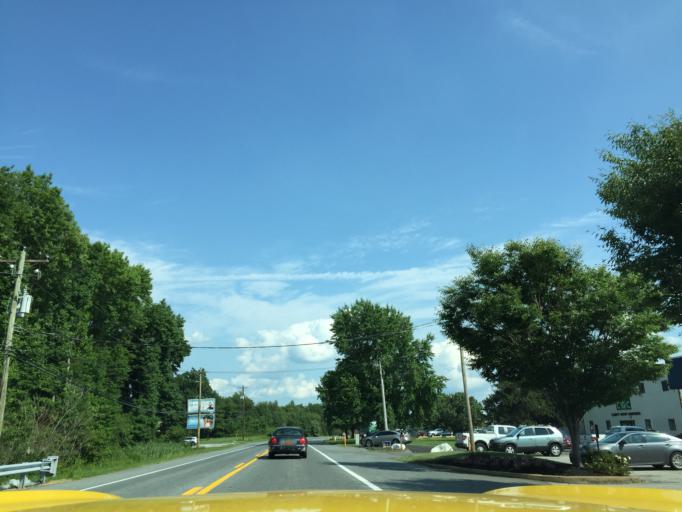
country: US
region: Delaware
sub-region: New Castle County
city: Wilmington Manor
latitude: 39.6698
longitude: -75.6144
